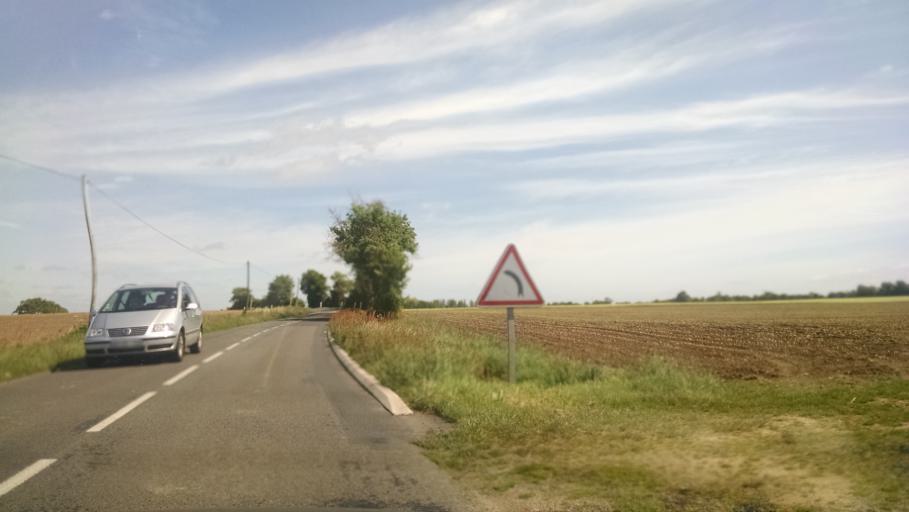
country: FR
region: Pays de la Loire
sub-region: Departement de la Loire-Atlantique
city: Saint-Hilaire-de-Clisson
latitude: 47.0429
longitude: -1.3236
